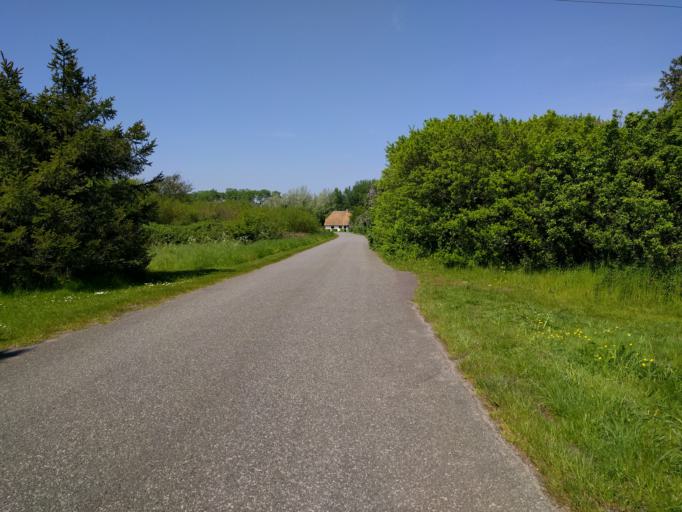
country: DK
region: Zealand
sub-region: Guldborgsund Kommune
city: Stubbekobing
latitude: 54.8843
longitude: 12.1197
